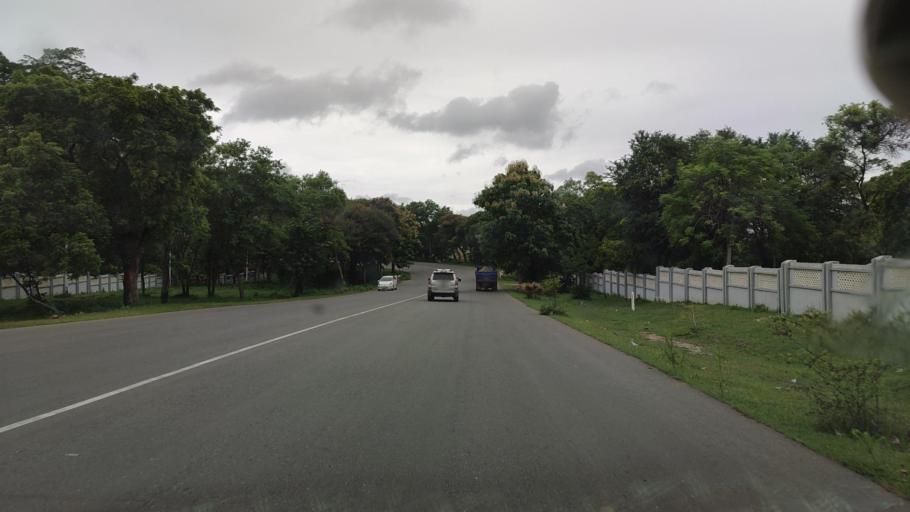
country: MM
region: Mandalay
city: Meiktila
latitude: 20.8526
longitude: 95.8823
